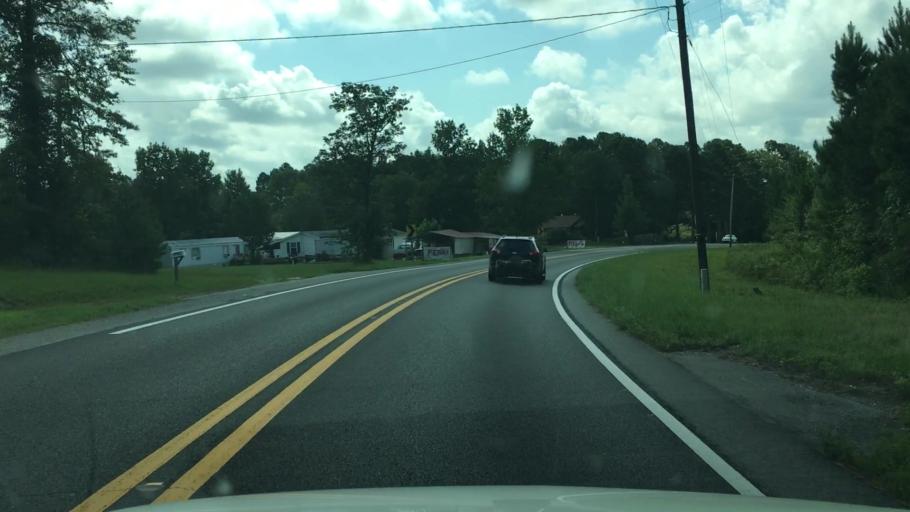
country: US
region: Arkansas
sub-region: Garland County
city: Lake Hamilton
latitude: 34.2776
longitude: -93.1518
